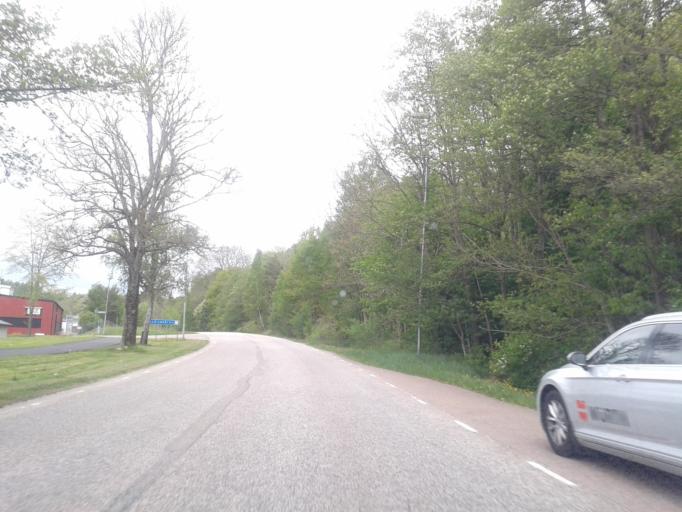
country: SE
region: Vaestra Goetaland
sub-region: Kungalvs Kommun
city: Kungalv
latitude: 57.8864
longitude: 11.9907
